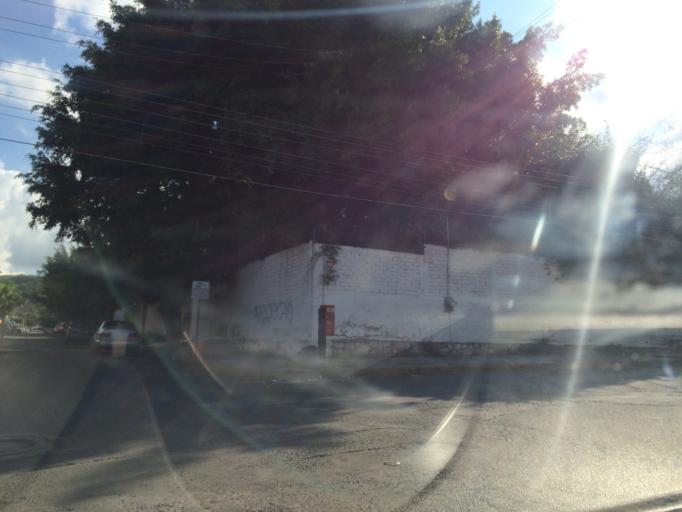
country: MX
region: Nayarit
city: Tepic
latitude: 21.5010
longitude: -104.9067
